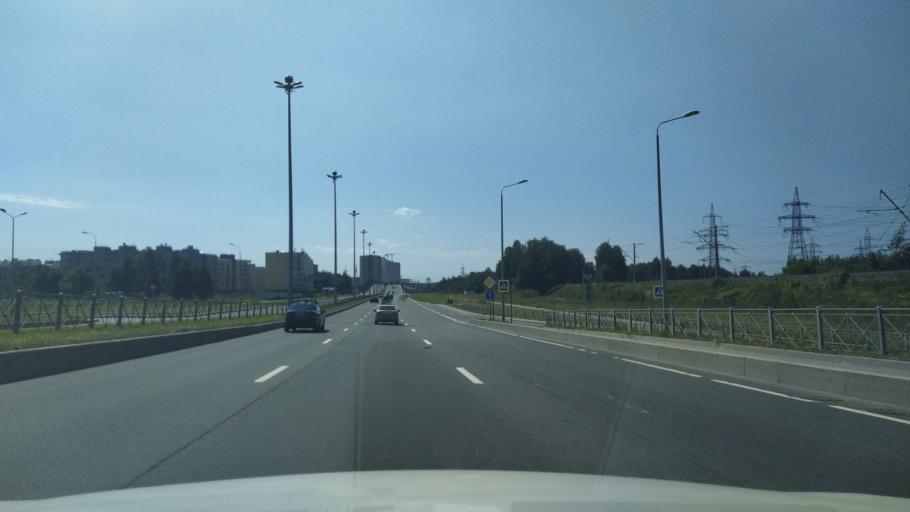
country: RU
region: St.-Petersburg
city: Shuvalovo
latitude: 60.0654
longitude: 30.2957
